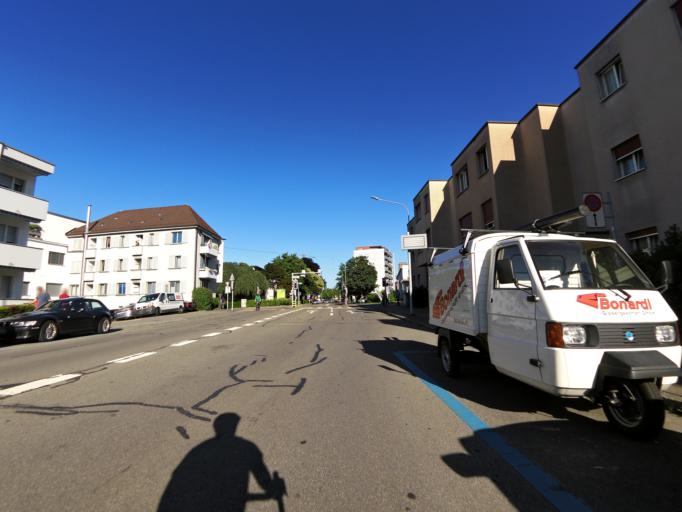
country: CH
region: Zurich
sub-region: Bezirk Zuerich
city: Zuerich (Kreis 4) / Hard
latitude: 47.3854
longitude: 8.5001
